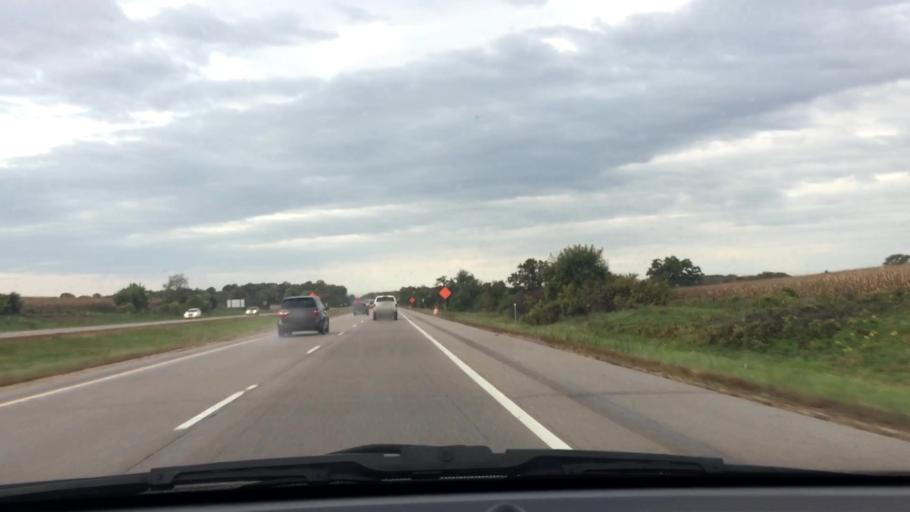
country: US
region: Wisconsin
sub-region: Rock County
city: Clinton
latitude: 42.5511
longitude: -88.9303
